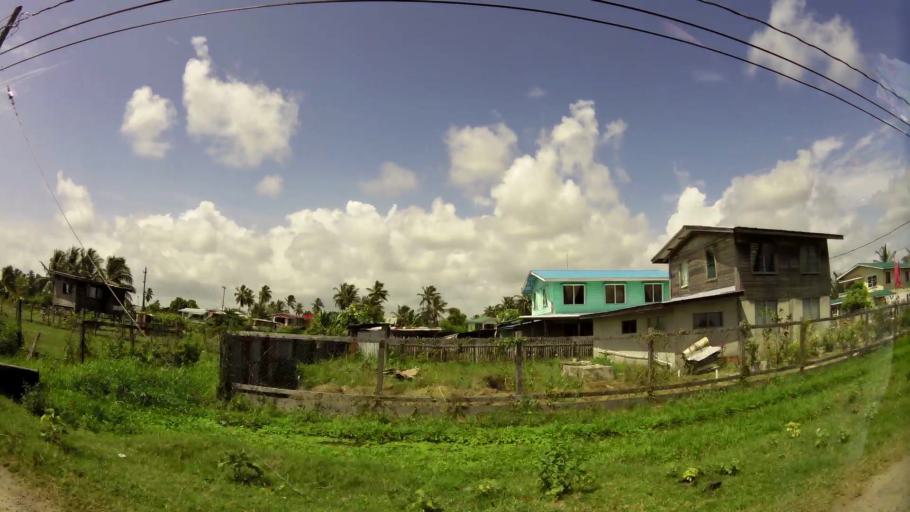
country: GY
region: Demerara-Mahaica
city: Mahaica Village
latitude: 6.7692
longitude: -58.0084
